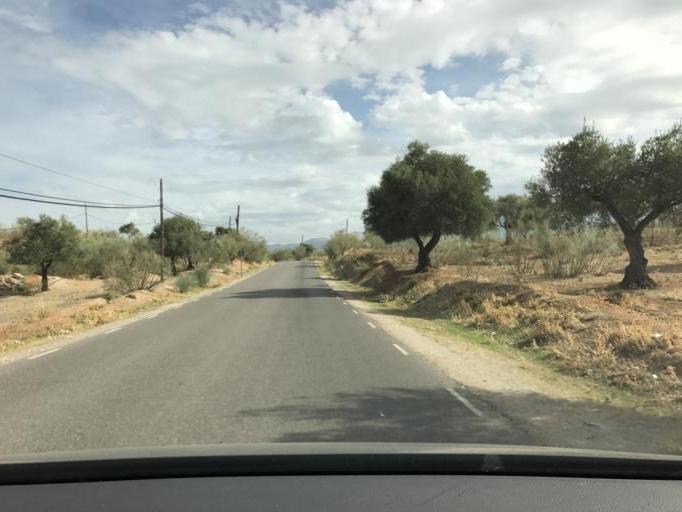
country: ES
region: Andalusia
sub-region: Provincia de Granada
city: Jun
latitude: 37.1969
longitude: -3.5742
